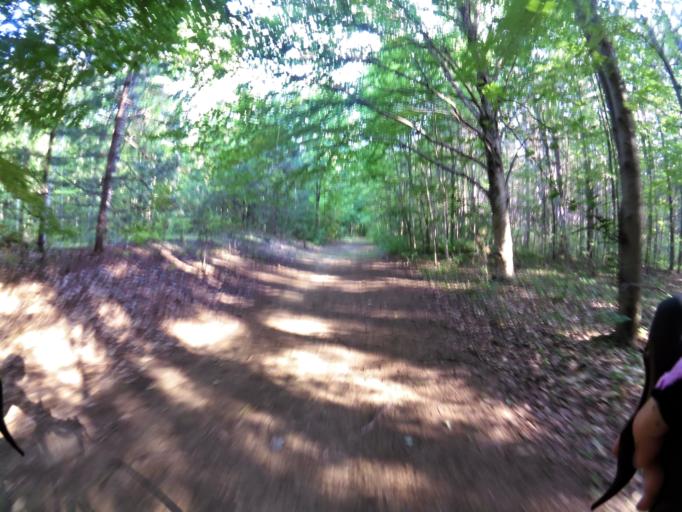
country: CA
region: Ontario
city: Bells Corners
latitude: 45.3175
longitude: -75.7358
